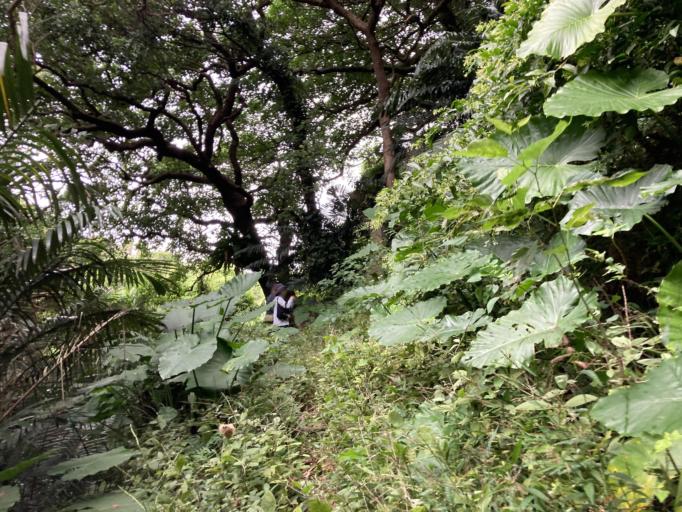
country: JP
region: Okinawa
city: Ishikawa
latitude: 26.3919
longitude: 127.7581
